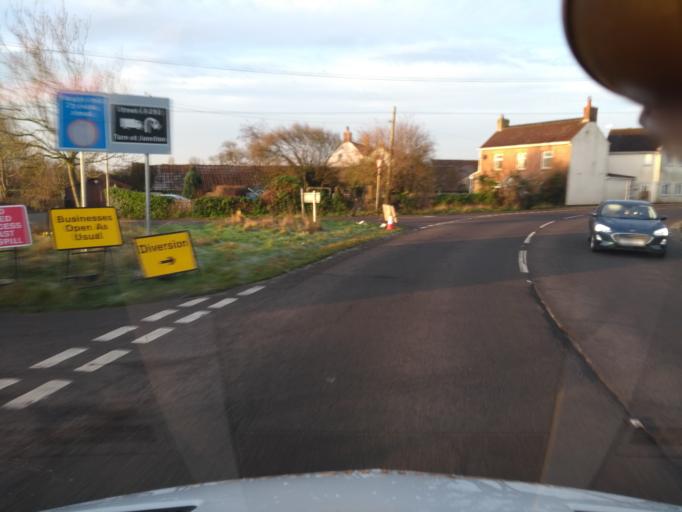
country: GB
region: England
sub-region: Somerset
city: Highbridge
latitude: 51.2164
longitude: -2.9395
